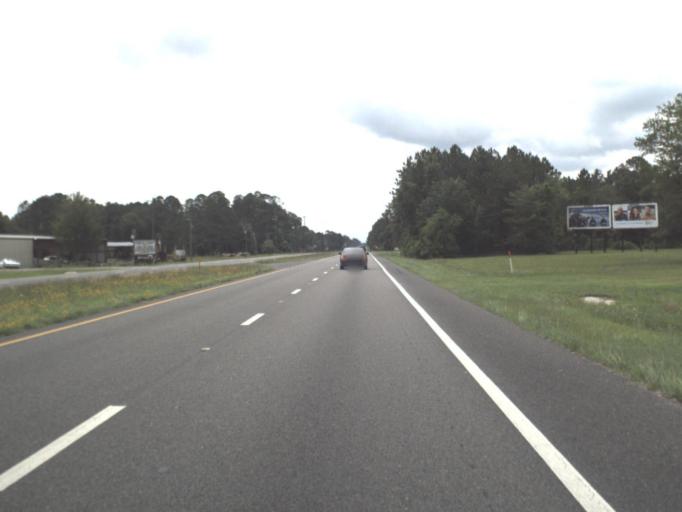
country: US
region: Florida
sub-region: Nassau County
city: Hilliard
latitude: 30.7211
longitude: -81.9388
